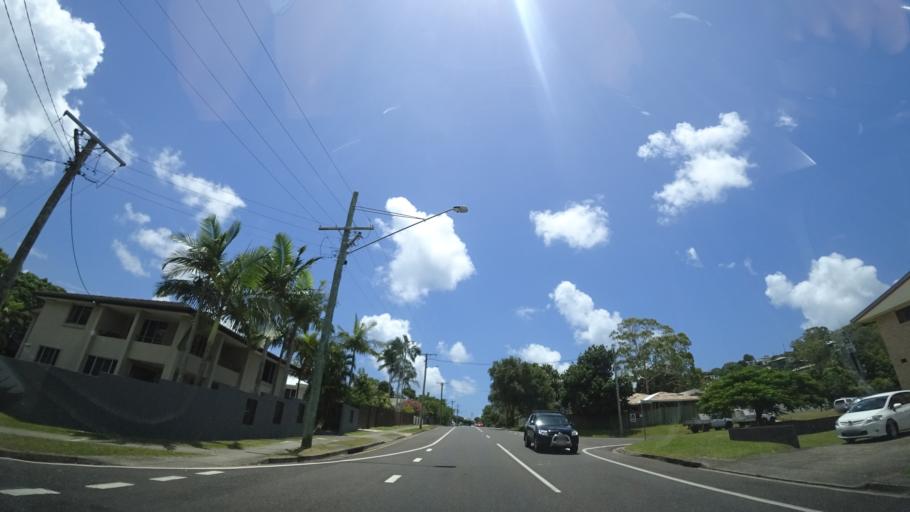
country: AU
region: Queensland
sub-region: Sunshine Coast
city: Coolum Beach
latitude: -26.5344
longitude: 153.0863
